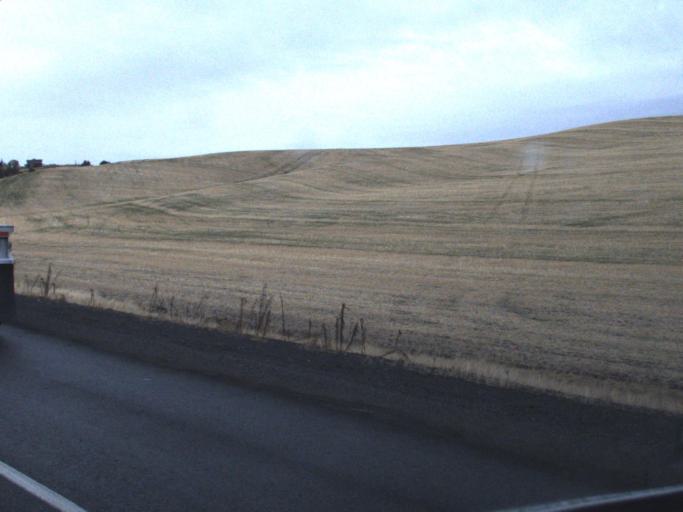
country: US
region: Washington
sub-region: Whitman County
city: Pullman
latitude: 46.7078
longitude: -117.2055
